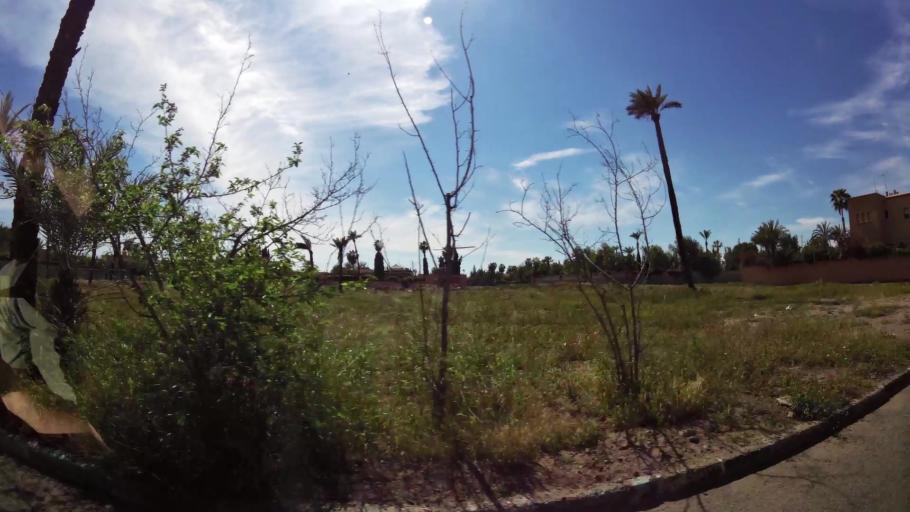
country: MA
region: Marrakech-Tensift-Al Haouz
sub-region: Marrakech
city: Marrakesh
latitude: 31.6432
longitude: -8.0490
